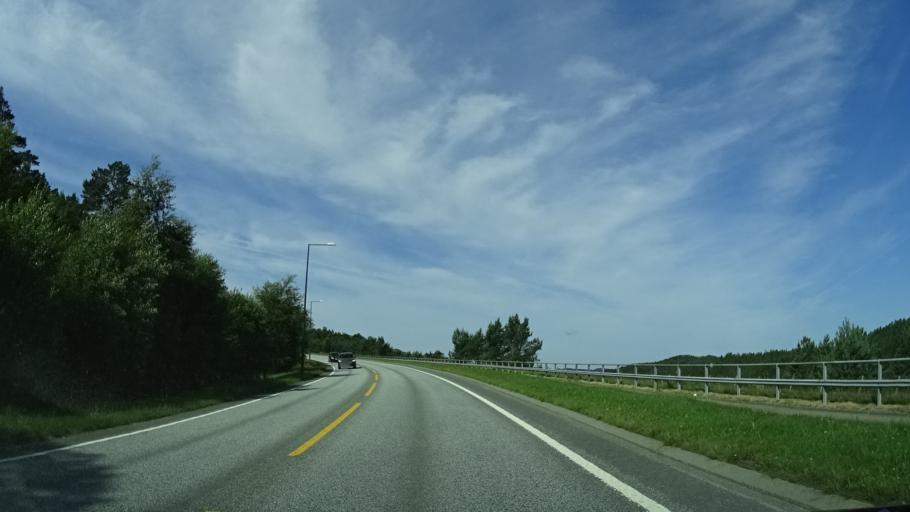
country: NO
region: Hordaland
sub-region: Stord
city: Sagvag
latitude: 59.7609
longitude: 5.4156
